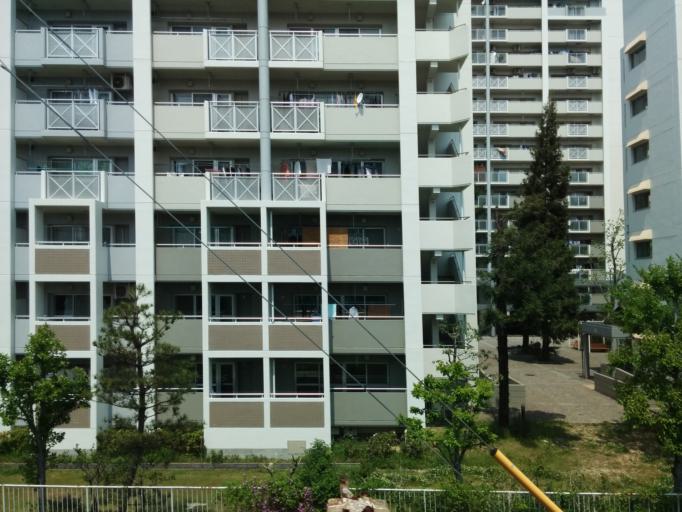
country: JP
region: Osaka
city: Suita
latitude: 34.7435
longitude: 135.5253
